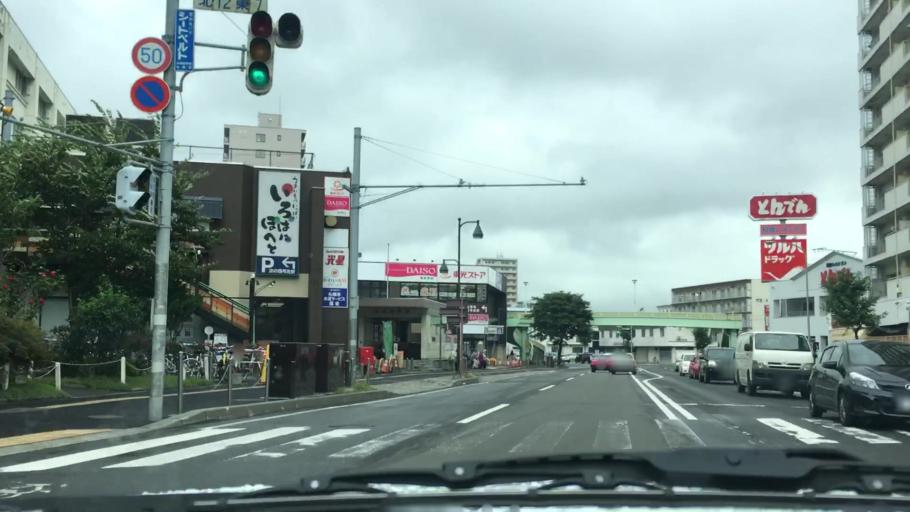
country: JP
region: Hokkaido
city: Sapporo
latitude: 43.0770
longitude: 141.3641
